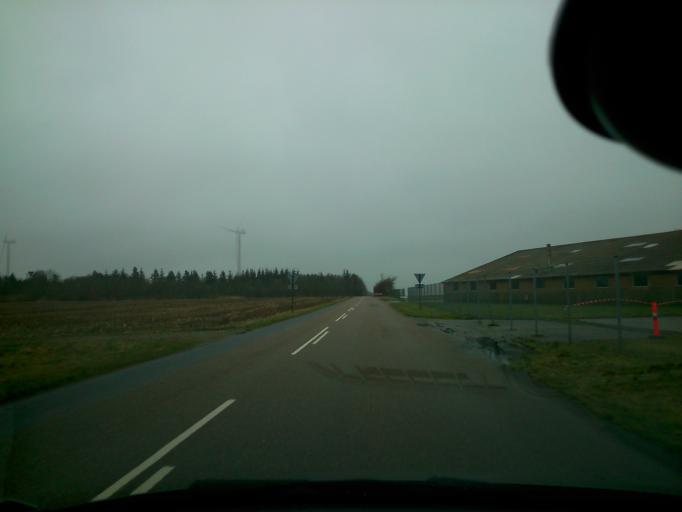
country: DK
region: Central Jutland
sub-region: Ringkobing-Skjern Kommune
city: Ringkobing
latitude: 56.0840
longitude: 8.3959
